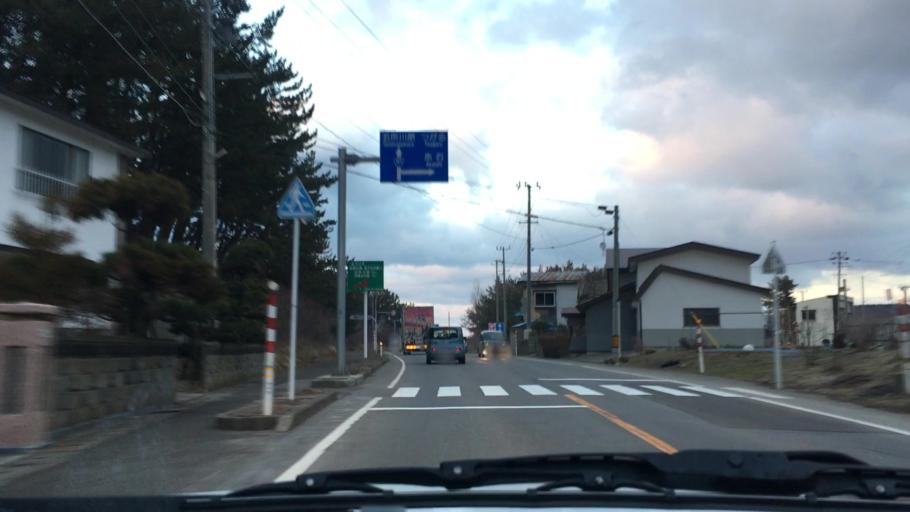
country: JP
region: Aomori
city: Shimokizukuri
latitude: 40.7574
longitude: 140.1544
